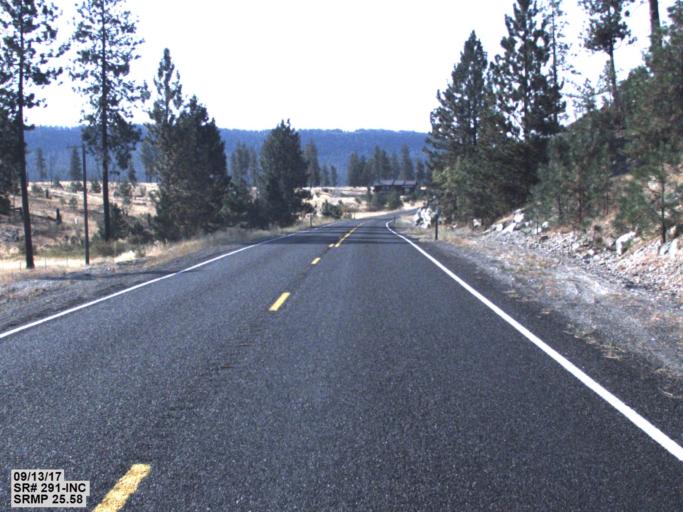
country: US
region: Washington
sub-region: Spokane County
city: Airway Heights
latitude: 47.8576
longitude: -117.7121
